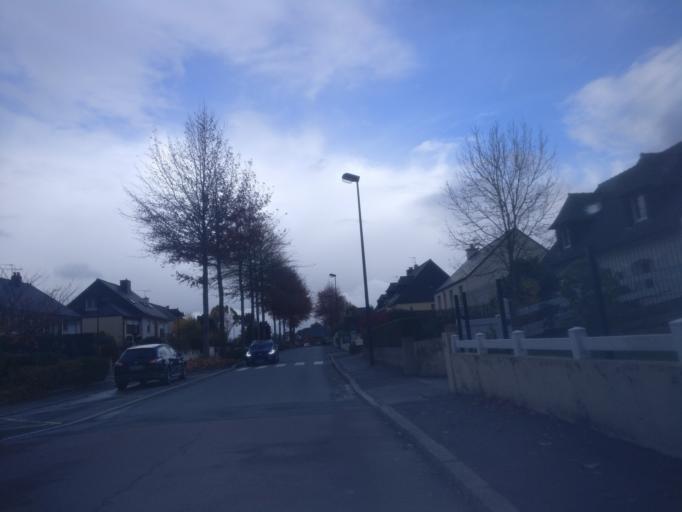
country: FR
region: Brittany
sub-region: Departement d'Ille-et-Vilaine
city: Breal-sous-Montfort
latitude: 48.0469
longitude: -1.8586
